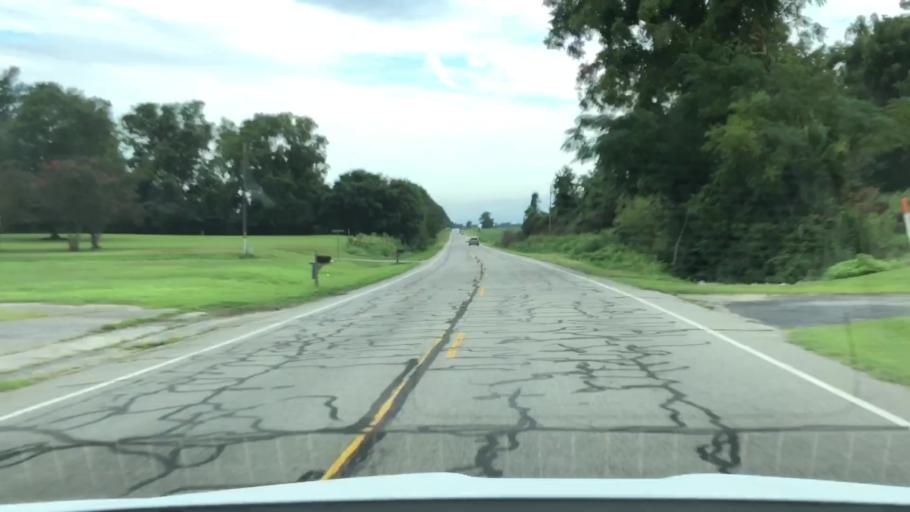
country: US
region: North Carolina
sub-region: Lenoir County
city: Kinston
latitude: 35.1386
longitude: -77.5298
